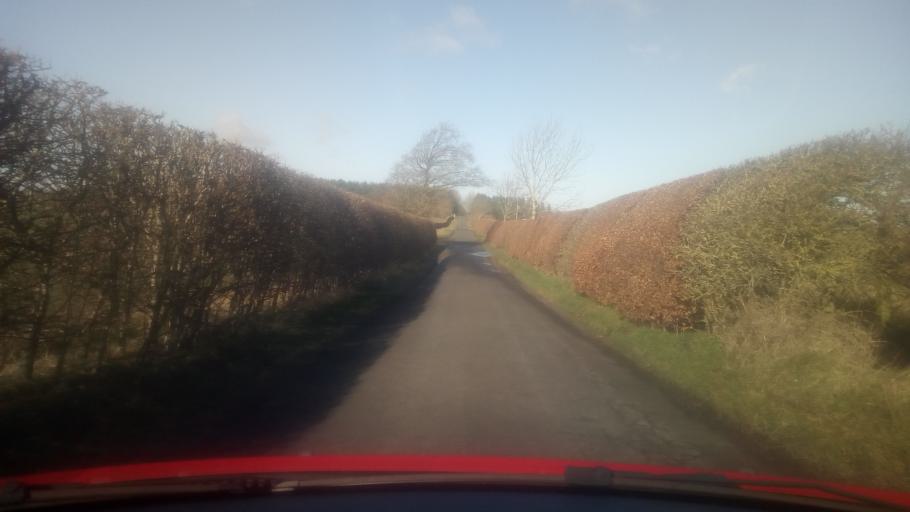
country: GB
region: Scotland
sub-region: The Scottish Borders
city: Saint Boswells
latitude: 55.5342
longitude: -2.6486
